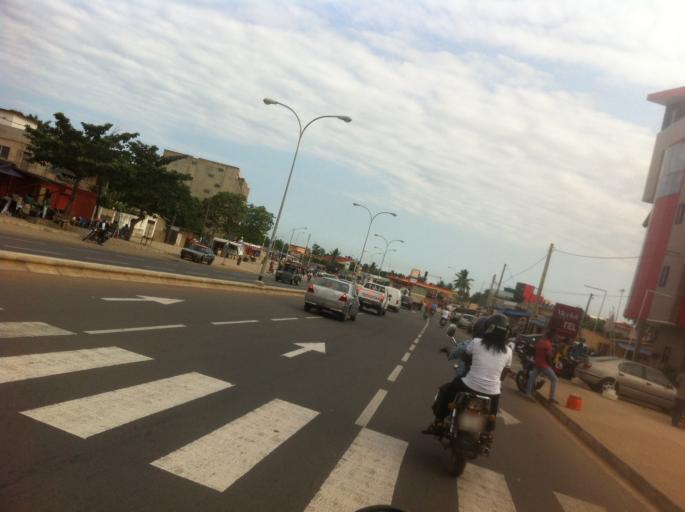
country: TG
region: Maritime
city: Lome
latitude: 6.1511
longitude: 1.2013
